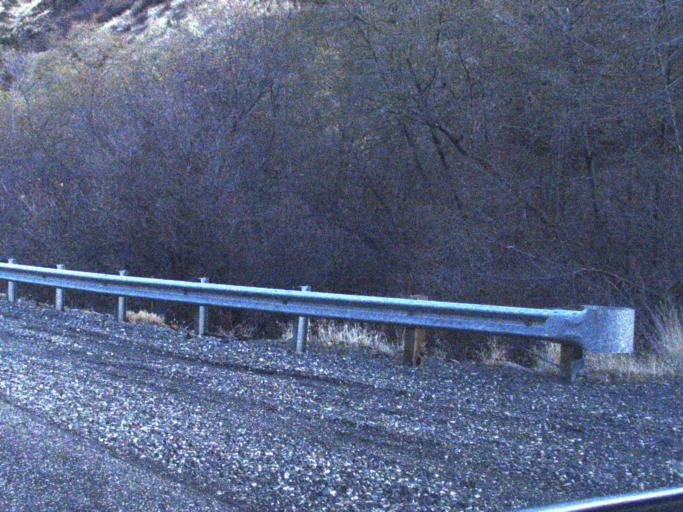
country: US
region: Washington
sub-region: Asotin County
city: Asotin
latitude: 46.0092
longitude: -117.2767
